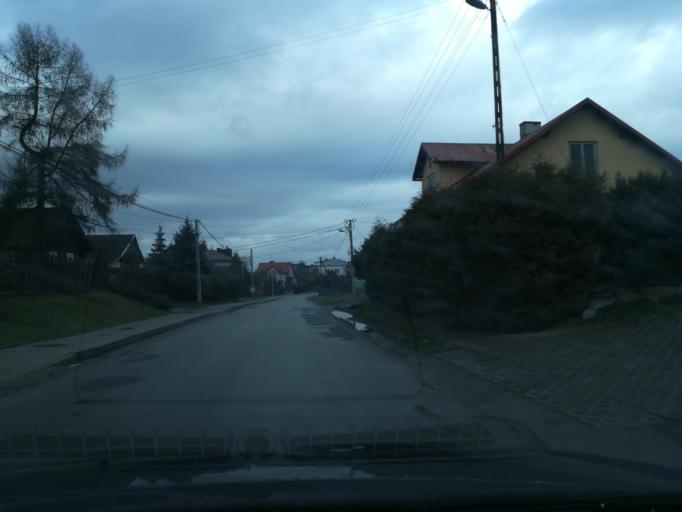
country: PL
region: Subcarpathian Voivodeship
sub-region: Powiat lancucki
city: Kosina
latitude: 50.0738
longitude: 22.3248
